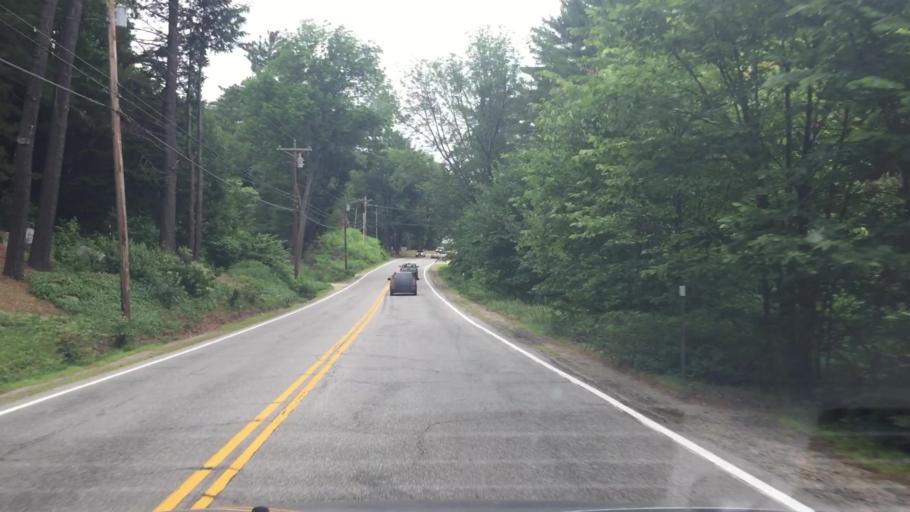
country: US
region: New Hampshire
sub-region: Carroll County
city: Center Harbor
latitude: 43.7279
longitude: -71.4277
